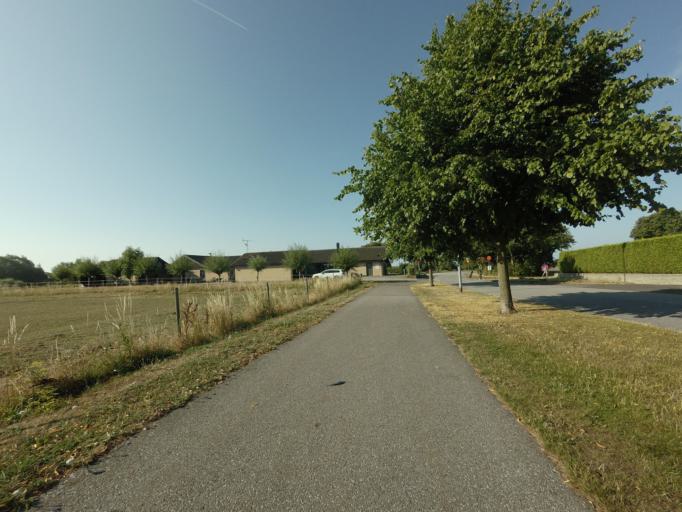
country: SE
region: Skane
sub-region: Trelleborgs Kommun
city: Trelleborg
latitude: 55.3608
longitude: 13.2257
